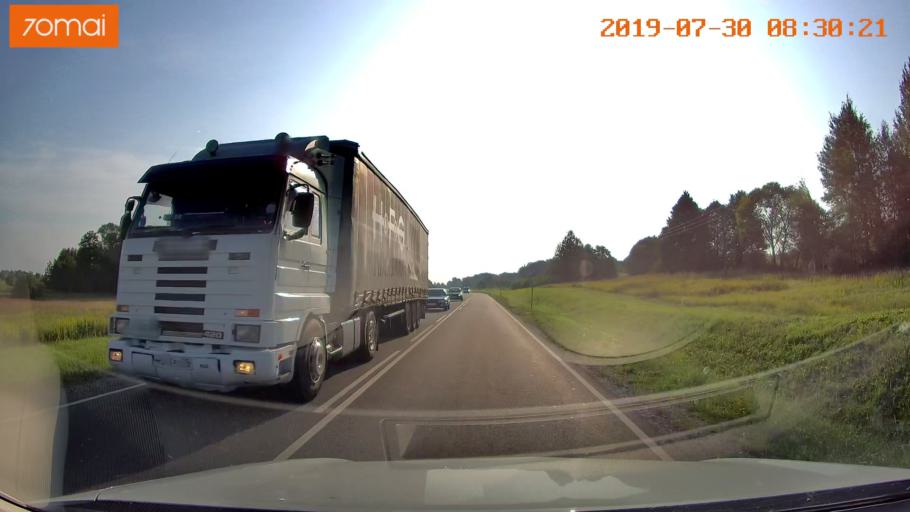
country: RU
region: Kaliningrad
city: Chernyakhovsk
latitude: 54.6338
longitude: 21.6834
